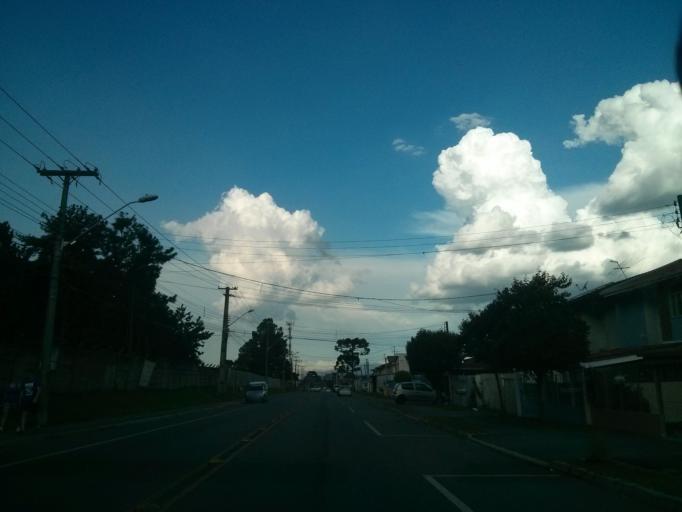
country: BR
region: Parana
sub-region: Sao Jose Dos Pinhais
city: Sao Jose dos Pinhais
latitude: -25.5116
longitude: -49.2362
